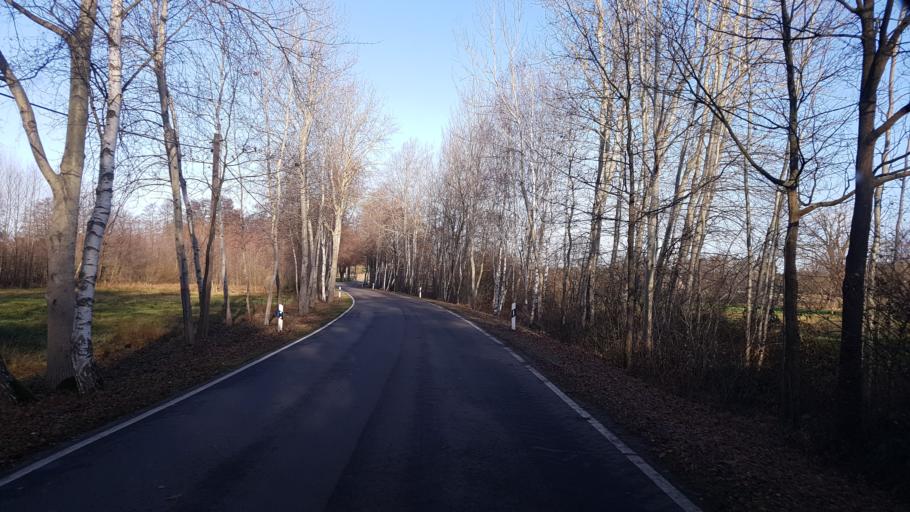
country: DE
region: Brandenburg
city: Ruckersdorf
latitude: 51.6051
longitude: 13.6006
